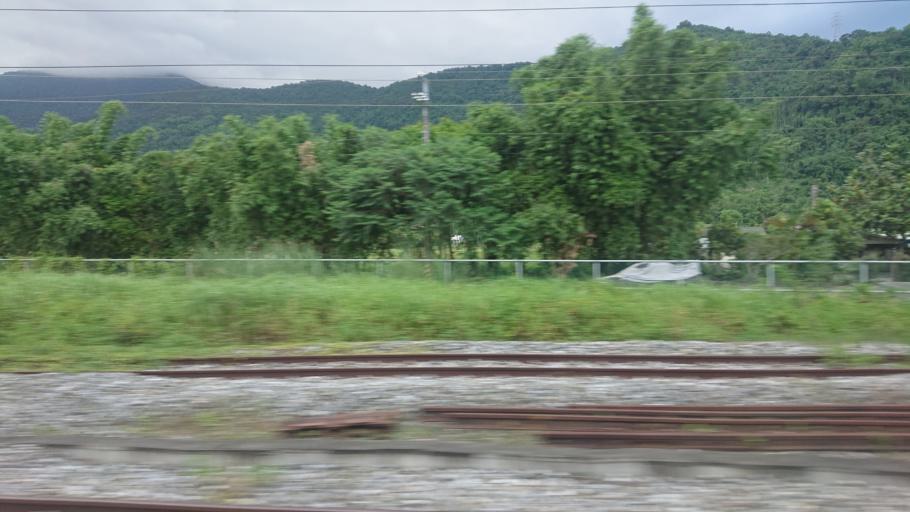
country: TW
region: Taiwan
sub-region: Hualien
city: Hualian
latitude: 23.6668
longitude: 121.4211
